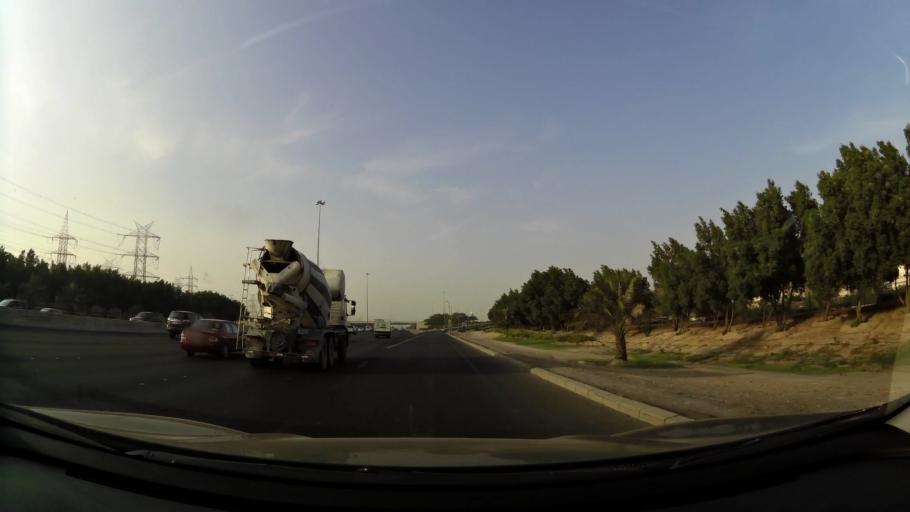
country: KW
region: Mubarak al Kabir
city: Sabah as Salim
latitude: 29.2354
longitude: 48.0514
